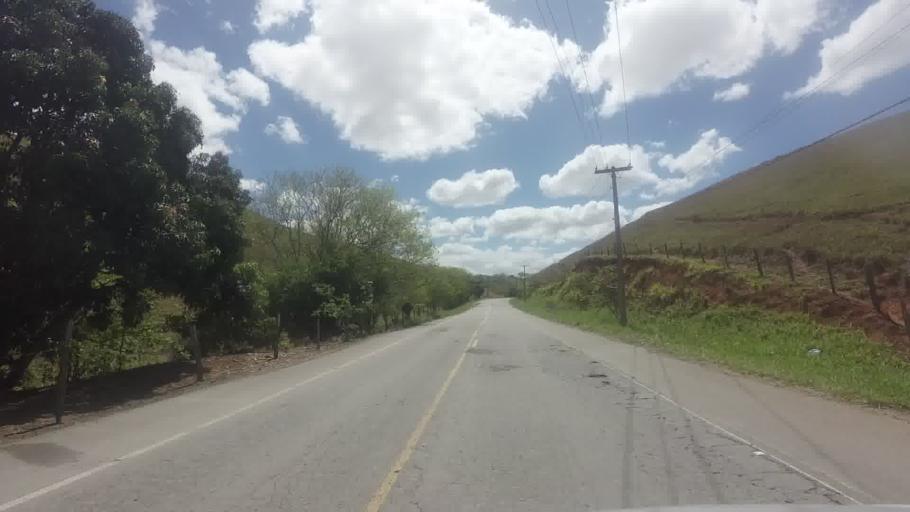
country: BR
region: Rio de Janeiro
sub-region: Santo Antonio De Padua
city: Santo Antonio de Padua
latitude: -21.6533
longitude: -42.2974
